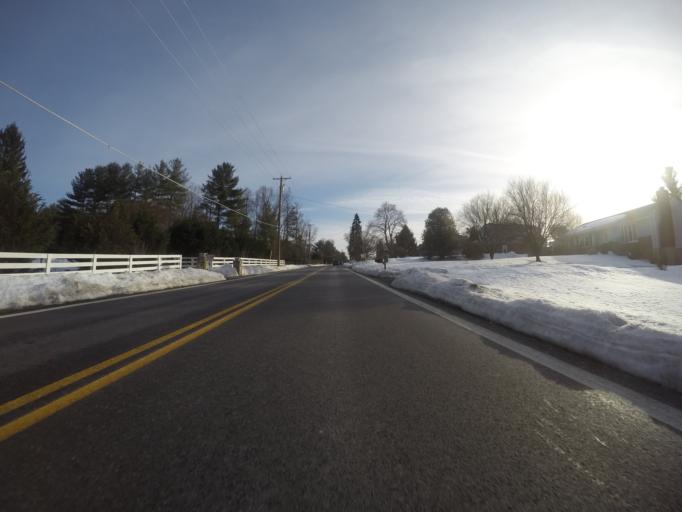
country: US
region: Maryland
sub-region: Baltimore County
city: Hampton
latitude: 39.4927
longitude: -76.5672
